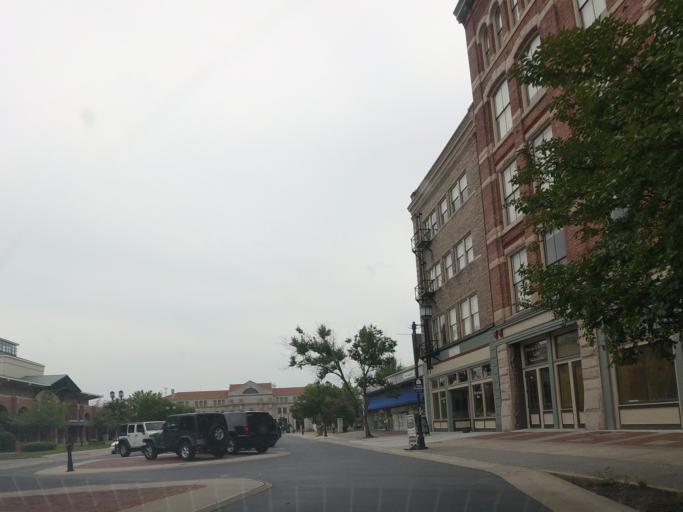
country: US
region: Georgia
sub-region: Bibb County
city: Macon
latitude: 32.8346
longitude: -83.6257
